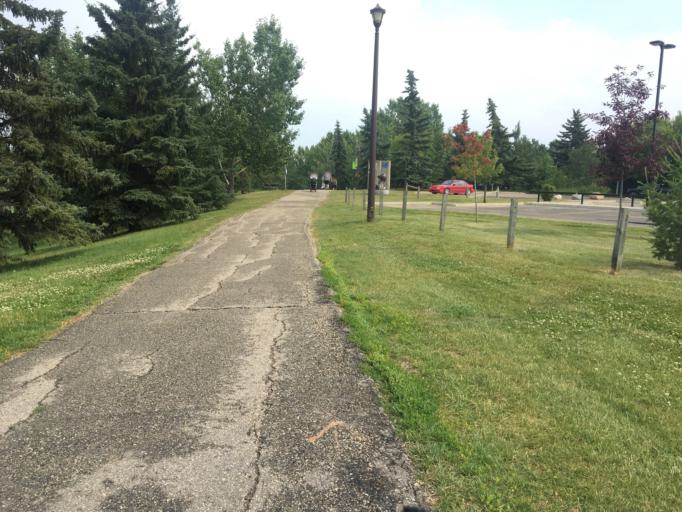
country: CA
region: Alberta
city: Grande Prairie
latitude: 55.1749
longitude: -118.8099
